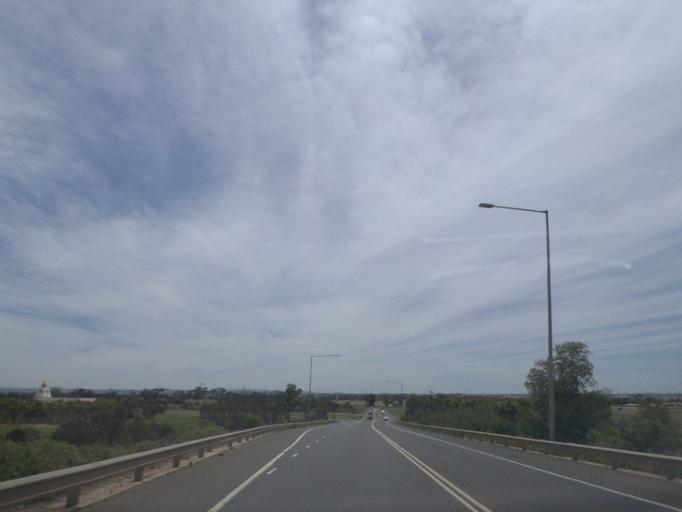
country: AU
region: Victoria
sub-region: Melton
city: Rockbank
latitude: -37.7446
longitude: 144.7005
